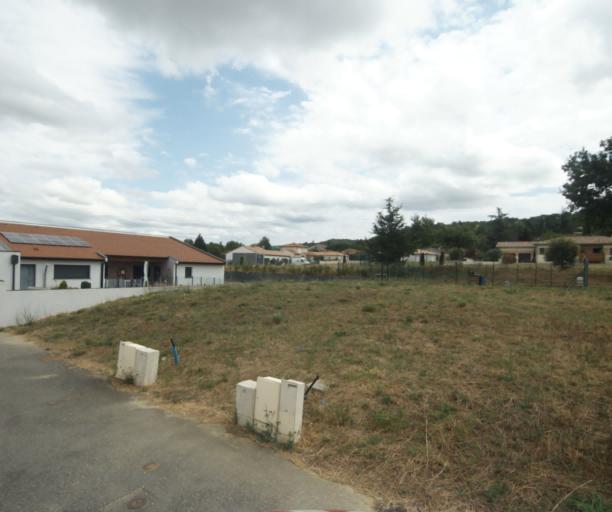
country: FR
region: Midi-Pyrenees
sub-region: Departement de la Haute-Garonne
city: Revel
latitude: 43.4499
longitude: 1.9940
